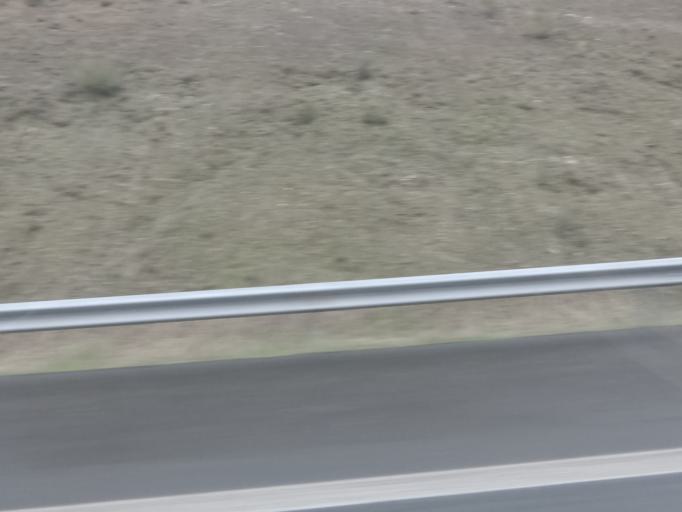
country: ES
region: Galicia
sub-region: Provincia da Coruna
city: Vedra
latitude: 42.8242
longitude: -8.5086
